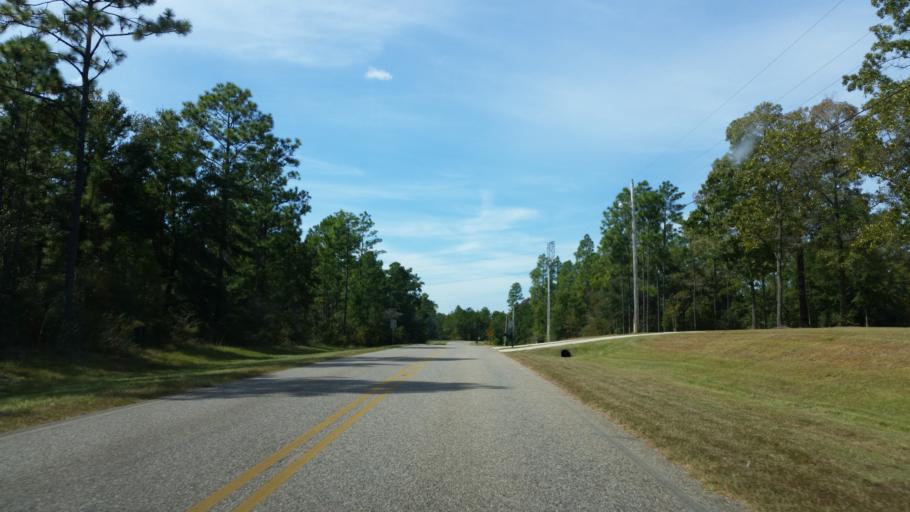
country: US
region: Alabama
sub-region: Baldwin County
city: Spanish Fort
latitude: 30.7358
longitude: -87.8530
